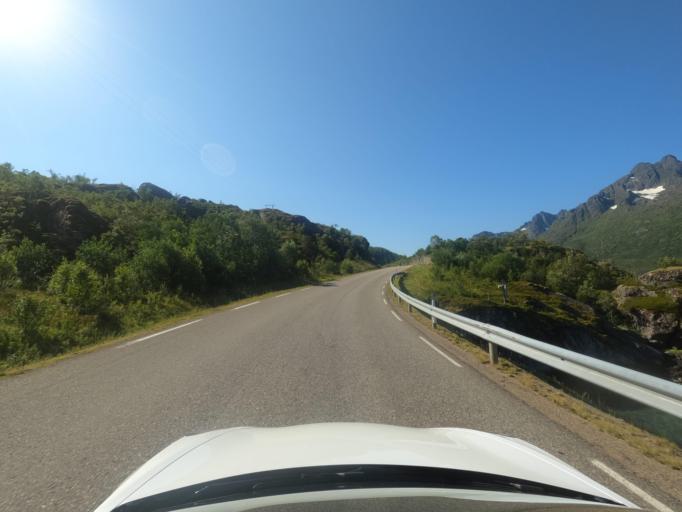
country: NO
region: Nordland
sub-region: Hadsel
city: Stokmarknes
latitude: 68.4382
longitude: 15.1851
